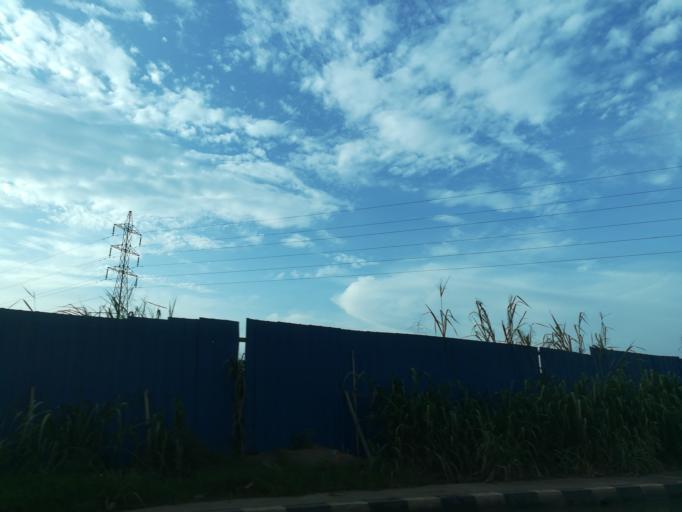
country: NG
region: Lagos
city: Ebute Ikorodu
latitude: 6.6188
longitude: 3.4619
